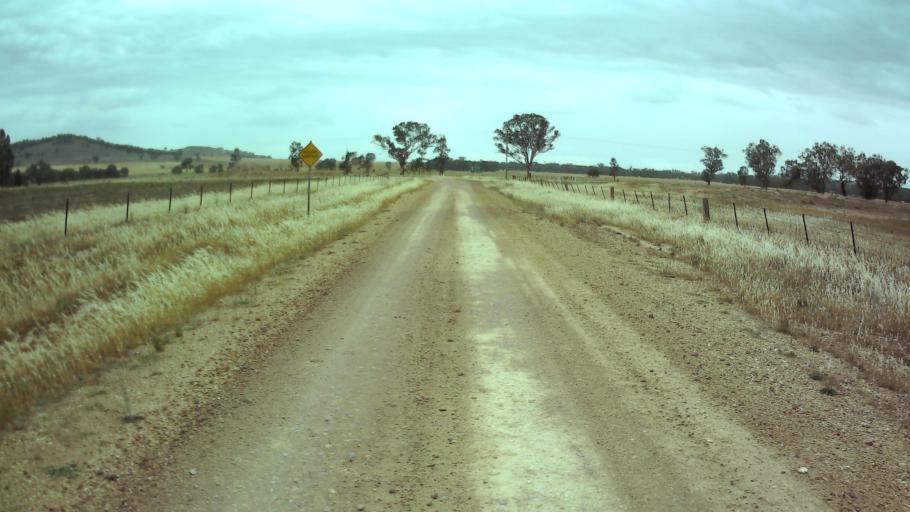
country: AU
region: New South Wales
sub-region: Weddin
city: Grenfell
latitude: -33.9314
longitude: 148.2792
